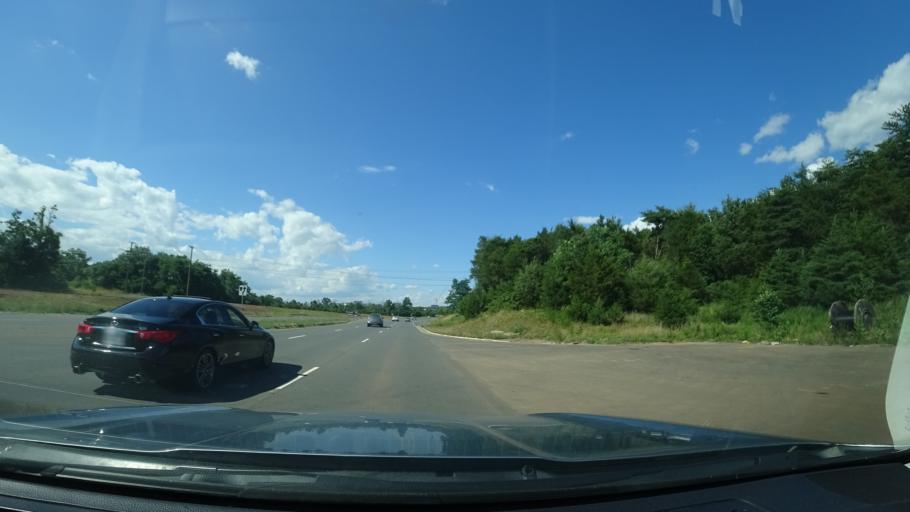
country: US
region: Virginia
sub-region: Loudoun County
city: Ashburn
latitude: 39.0031
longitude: -77.4747
